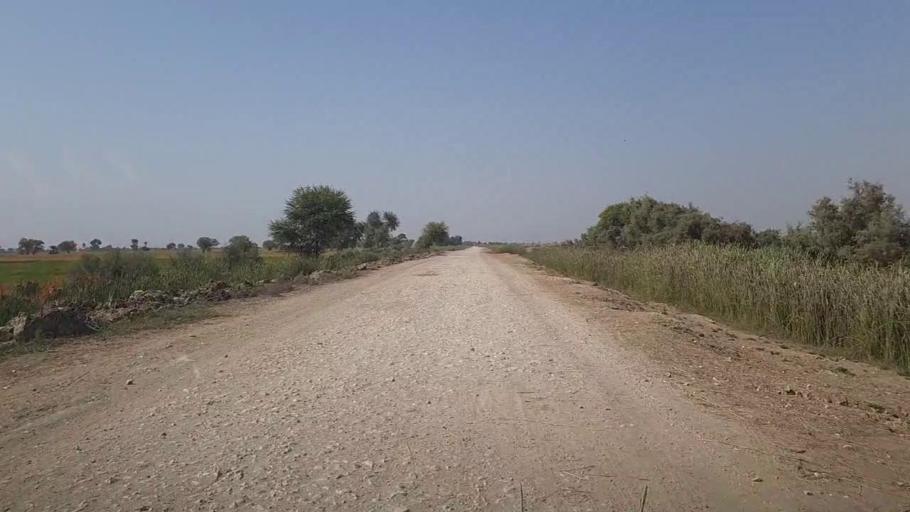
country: PK
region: Sindh
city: Kandhkot
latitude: 28.3956
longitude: 69.2732
